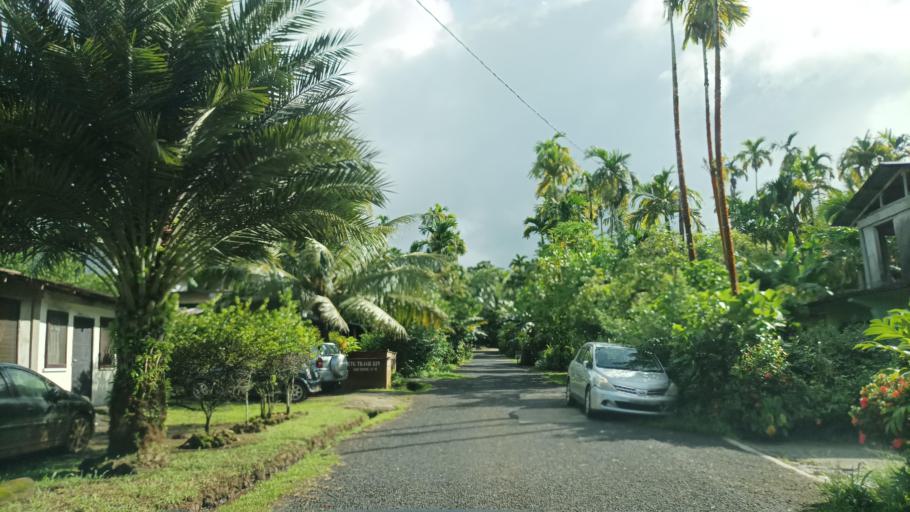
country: FM
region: Pohnpei
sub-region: Kolonia Municipality
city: Kolonia
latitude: 6.9678
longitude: 158.2066
